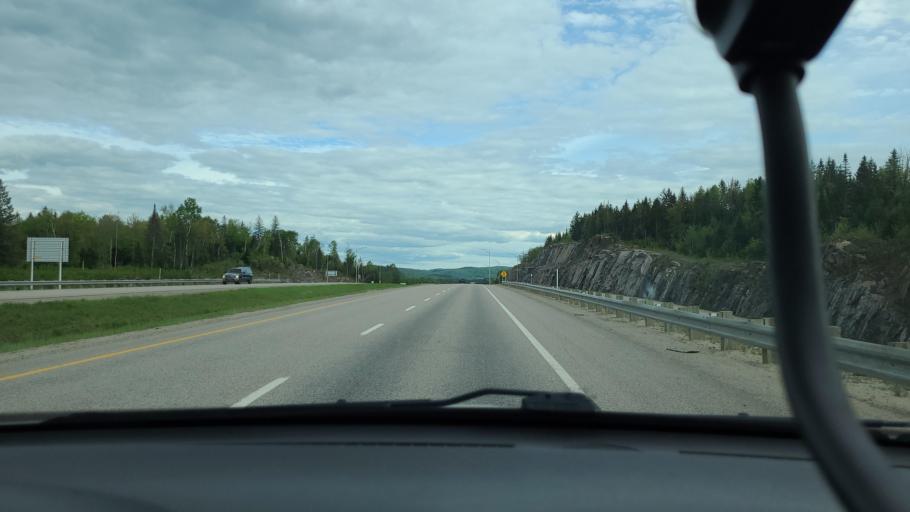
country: CA
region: Quebec
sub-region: Laurentides
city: Labelle
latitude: 46.2560
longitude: -74.7238
